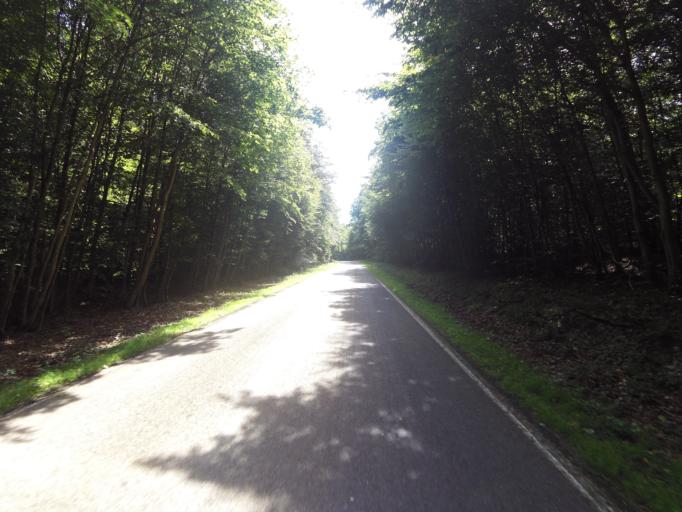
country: BE
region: Wallonia
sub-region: Province du Luxembourg
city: Nassogne
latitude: 50.0772
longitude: 5.3443
